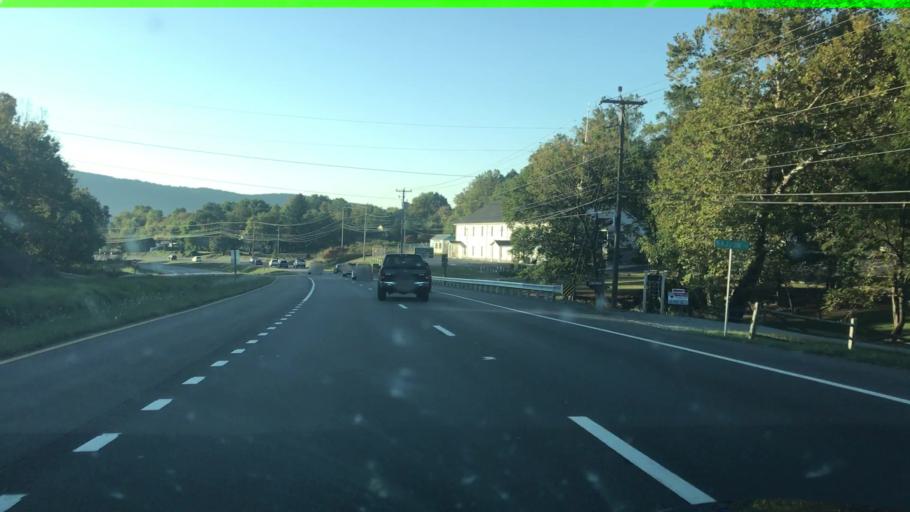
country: US
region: Virginia
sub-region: Botetourt County
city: Cloverdale
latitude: 37.3463
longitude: -79.8825
